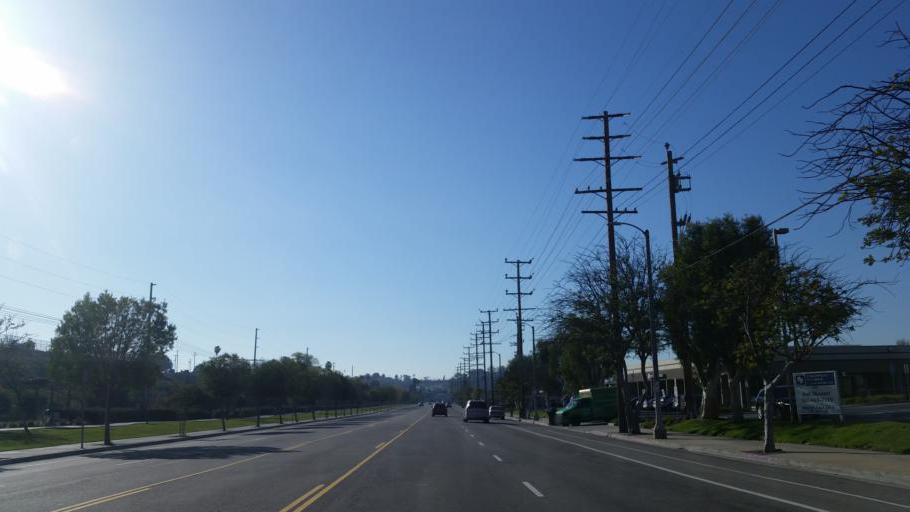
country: US
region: California
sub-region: Los Angeles County
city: San Pedro
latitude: 33.7627
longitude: -118.2932
